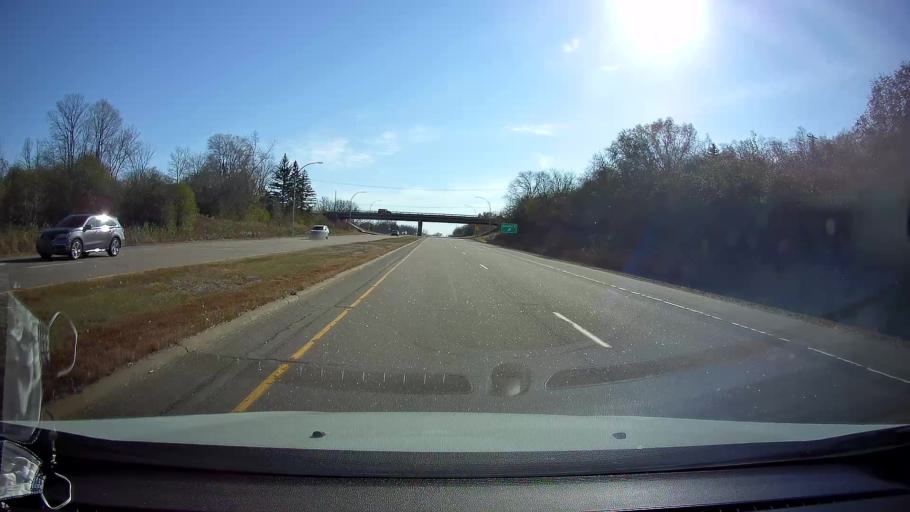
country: US
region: Minnesota
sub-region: Ramsey County
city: Arden Hills
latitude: 45.0519
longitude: -93.1569
